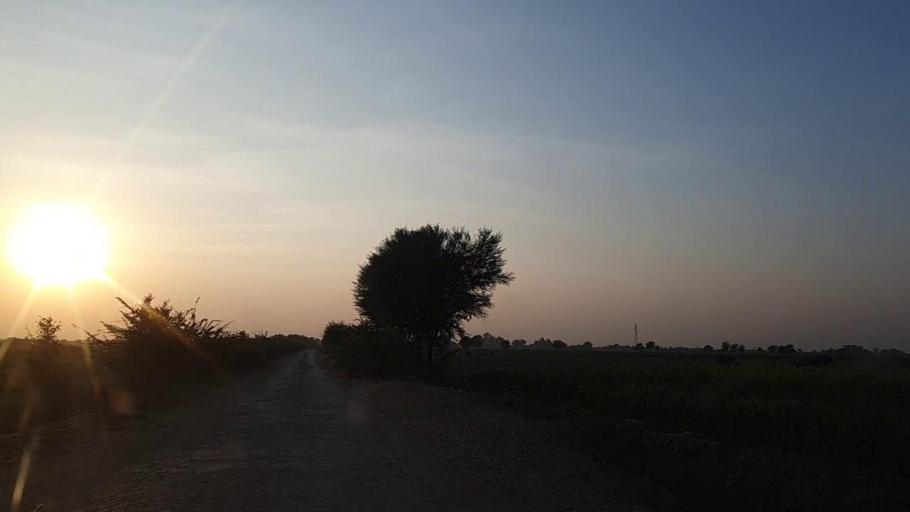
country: PK
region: Sindh
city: Naukot
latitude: 24.9472
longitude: 69.4401
